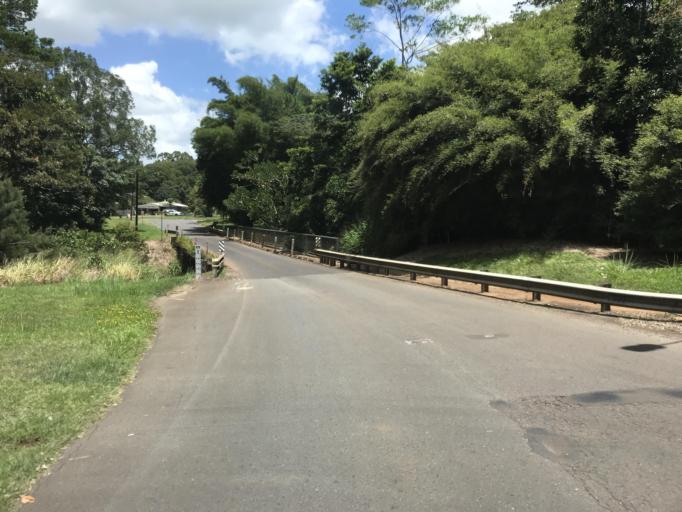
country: AU
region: Queensland
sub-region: Tablelands
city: Atherton
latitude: -17.3474
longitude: 145.5966
